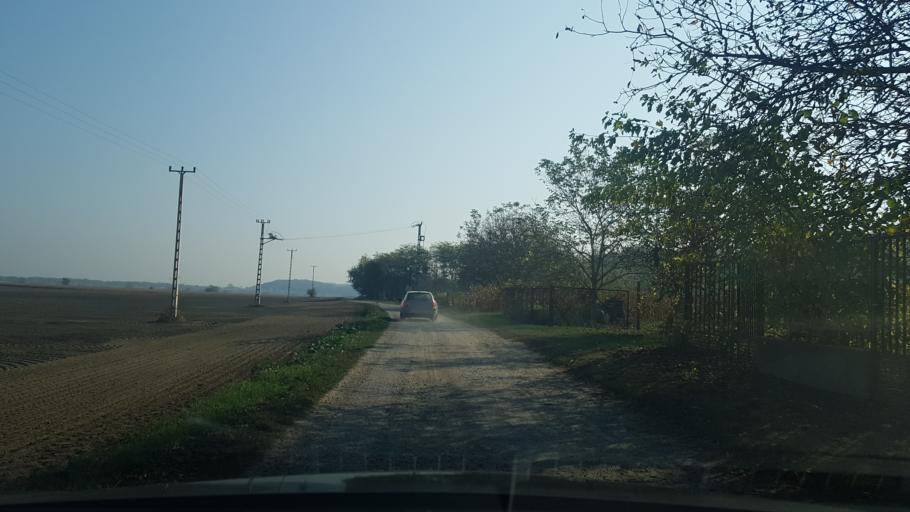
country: HU
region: Fejer
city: Adony
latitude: 47.0820
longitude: 18.8531
